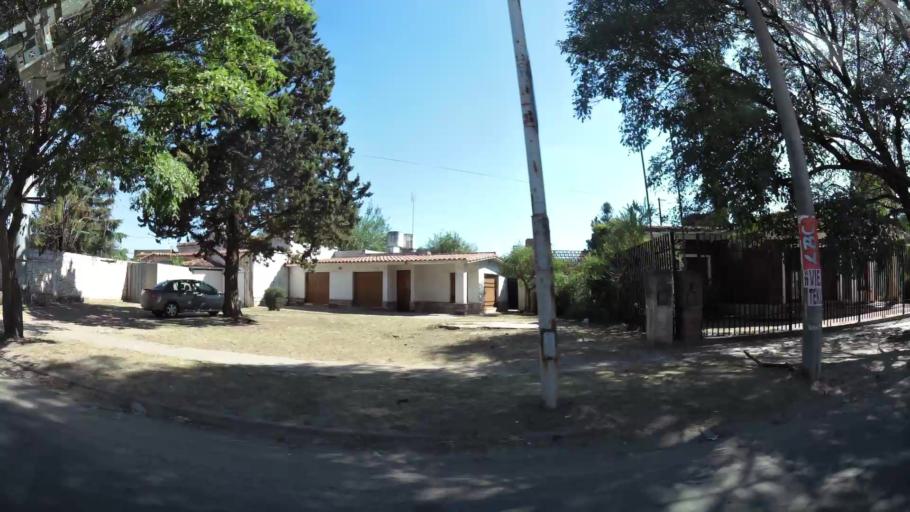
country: AR
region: Cordoba
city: Villa Allende
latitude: -31.3313
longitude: -64.2642
